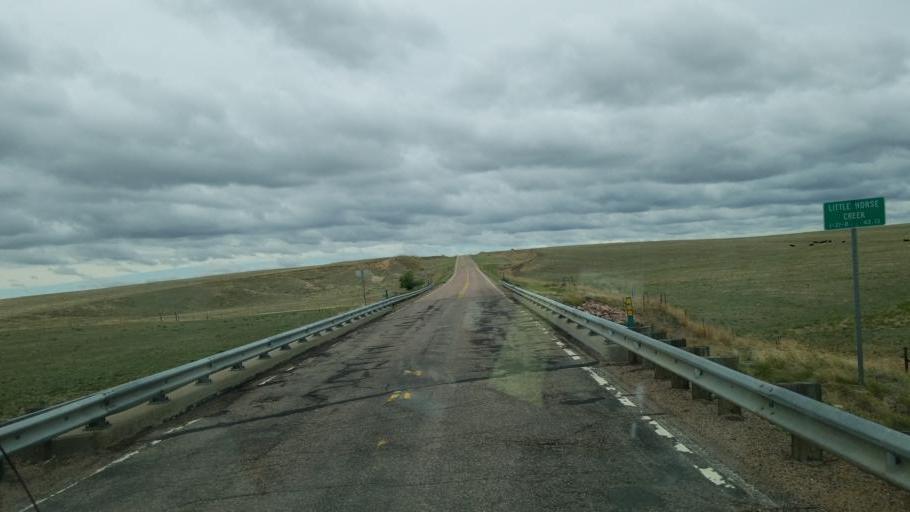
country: US
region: Colorado
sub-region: Lincoln County
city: Limon
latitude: 38.8393
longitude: -103.9048
